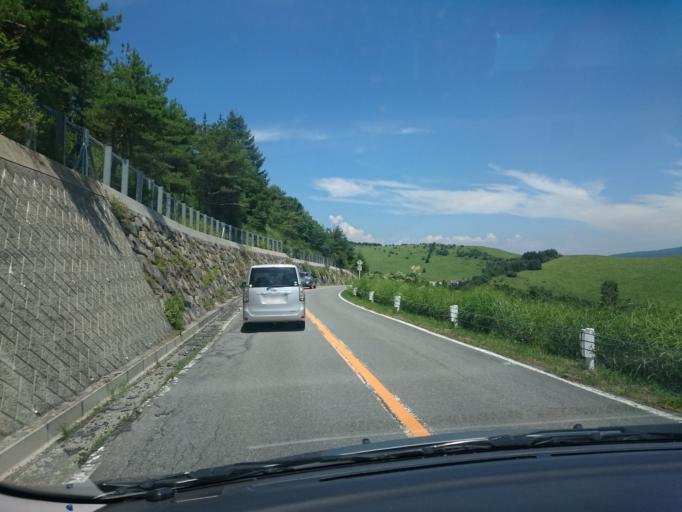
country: JP
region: Nagano
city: Suwa
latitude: 36.0967
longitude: 138.2090
